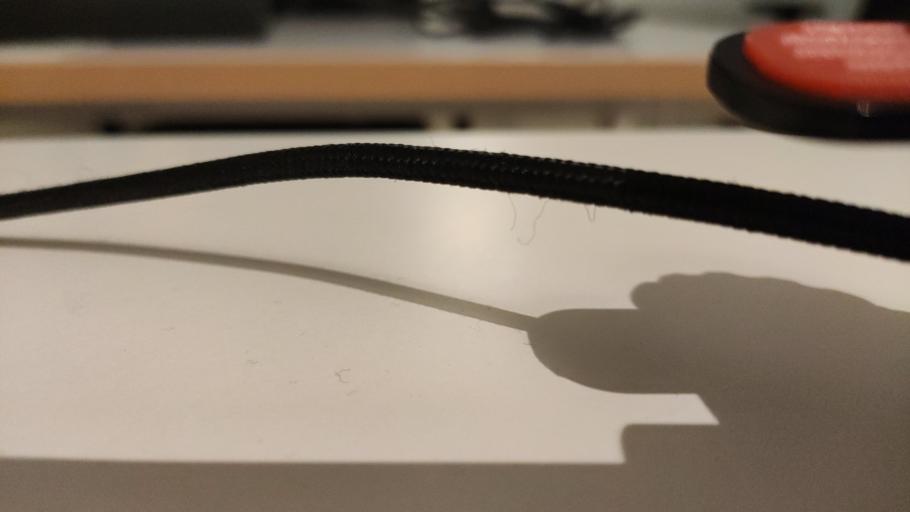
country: RU
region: Moskovskaya
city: Novosin'kovo
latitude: 56.3987
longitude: 37.2636
